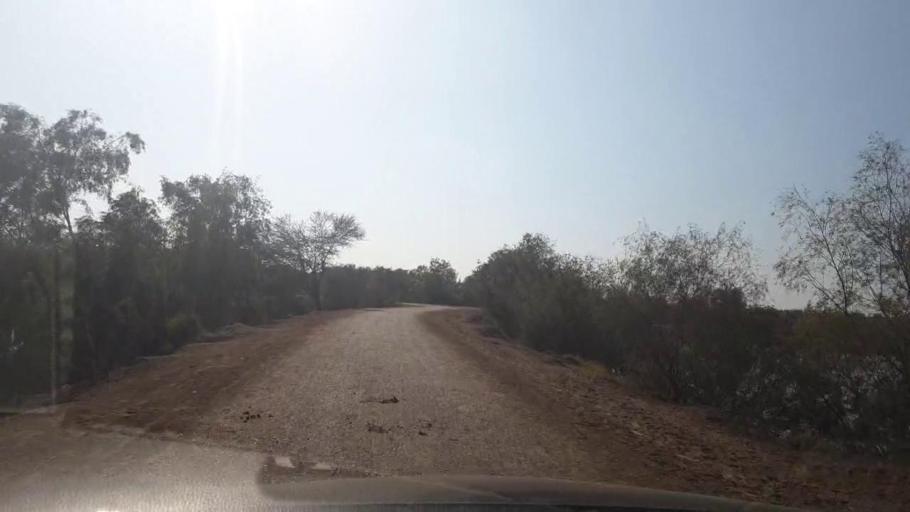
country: PK
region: Sindh
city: Khairpur
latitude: 28.1383
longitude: 69.6007
